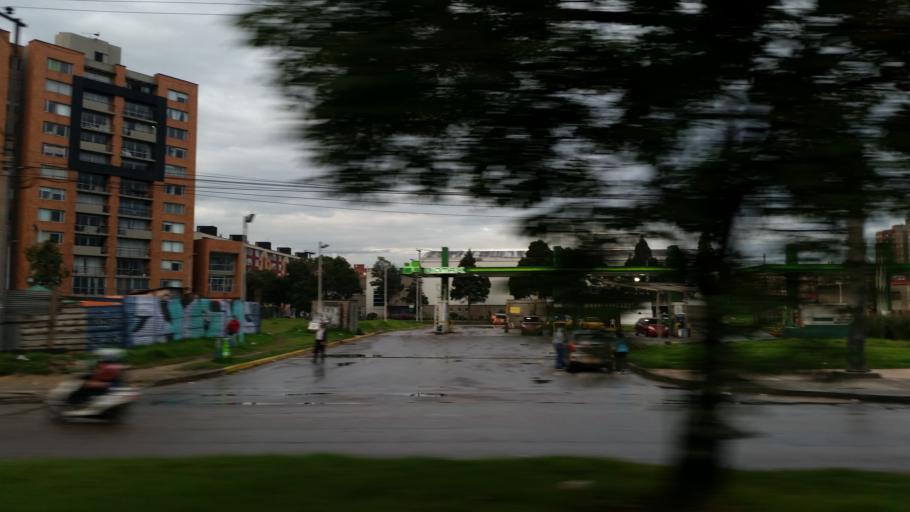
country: CO
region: Bogota D.C.
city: Bogota
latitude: 4.6620
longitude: -74.1382
